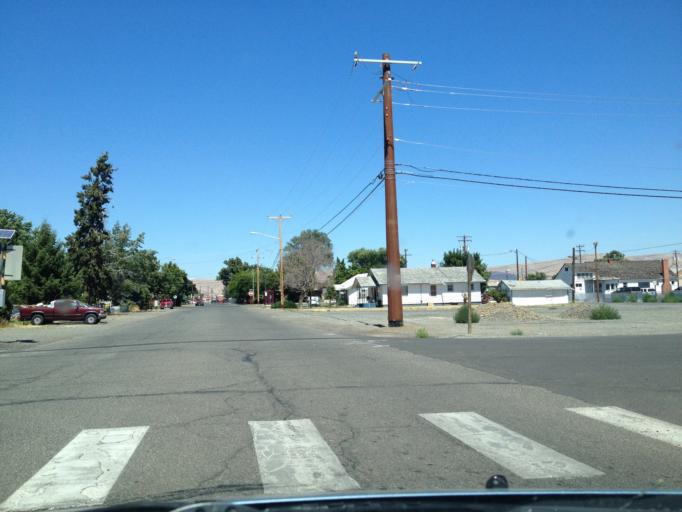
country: US
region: Washington
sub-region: Yakima County
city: Union Gap
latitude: 46.5559
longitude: -120.4778
